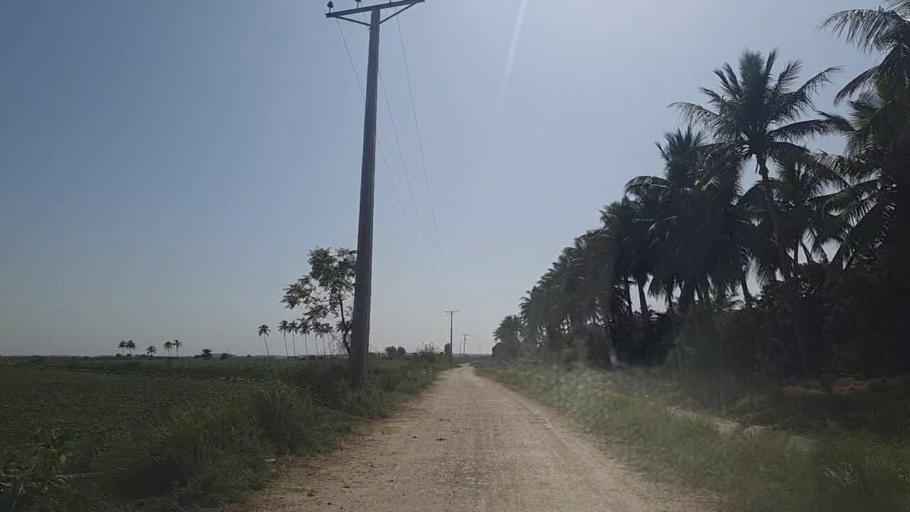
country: PK
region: Sindh
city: Thatta
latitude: 24.6363
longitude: 67.8865
